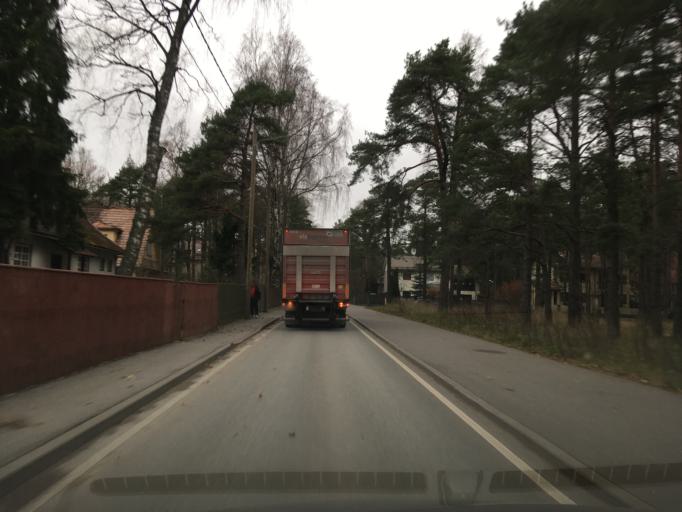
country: EE
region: Harju
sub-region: Saue vald
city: Laagri
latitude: 59.3781
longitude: 24.6763
